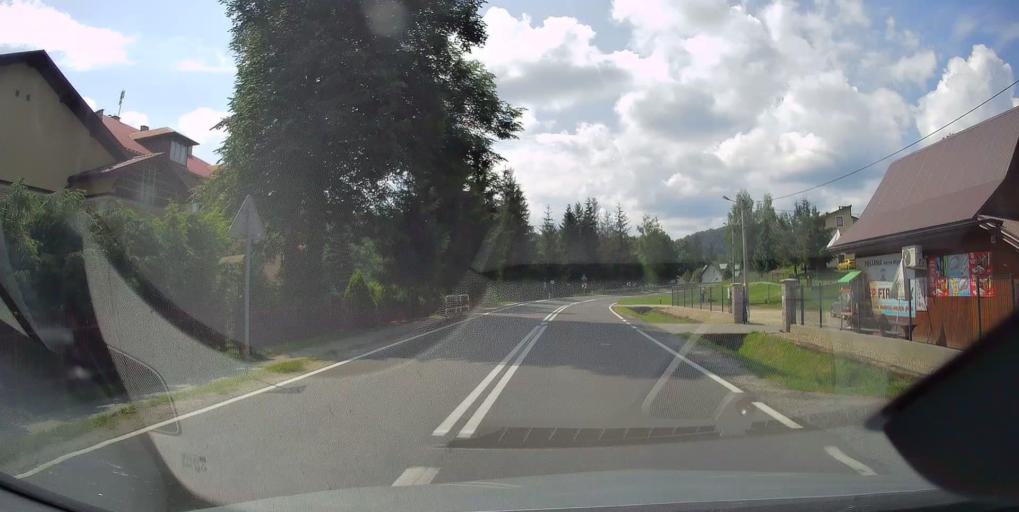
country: PL
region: Lesser Poland Voivodeship
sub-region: Powiat tarnowski
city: Zakliczyn
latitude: 49.7932
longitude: 20.8005
